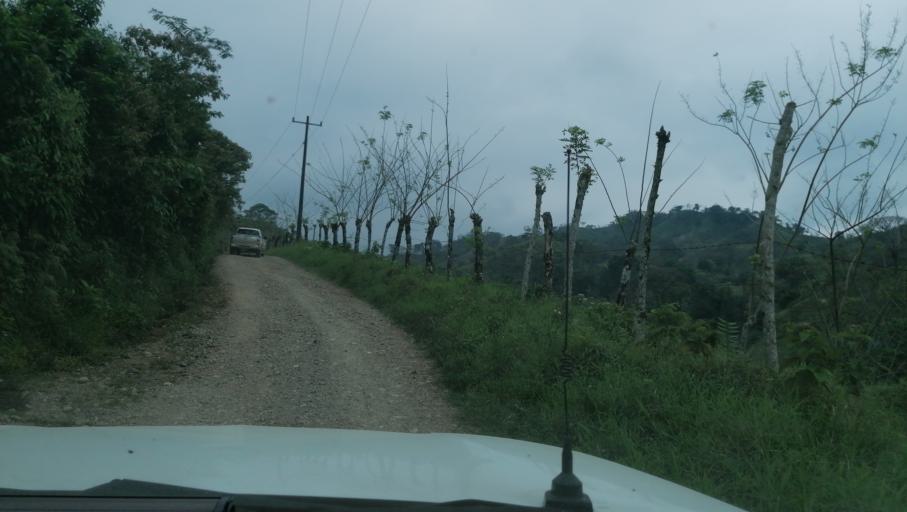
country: MX
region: Chiapas
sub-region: Francisco Leon
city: San Miguel la Sardina
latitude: 17.3284
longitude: -93.3115
